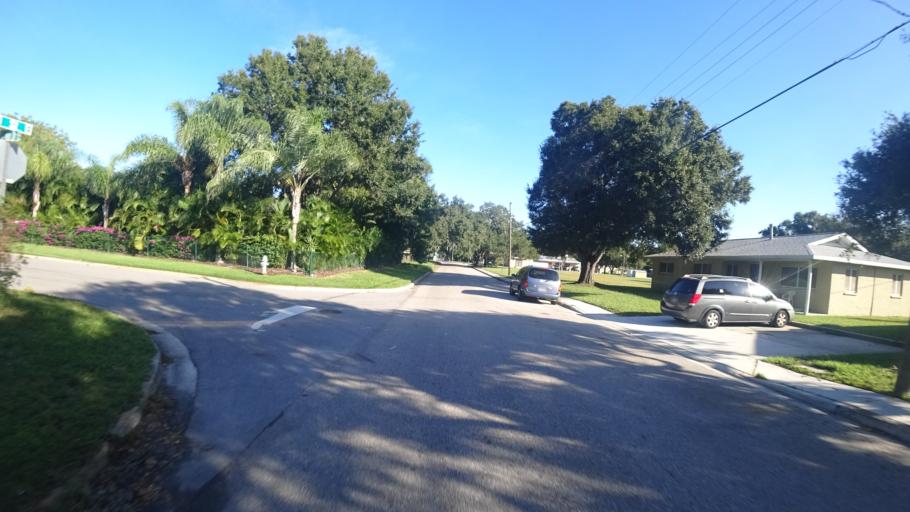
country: US
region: Florida
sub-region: Manatee County
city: Samoset
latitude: 27.4902
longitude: -82.5395
